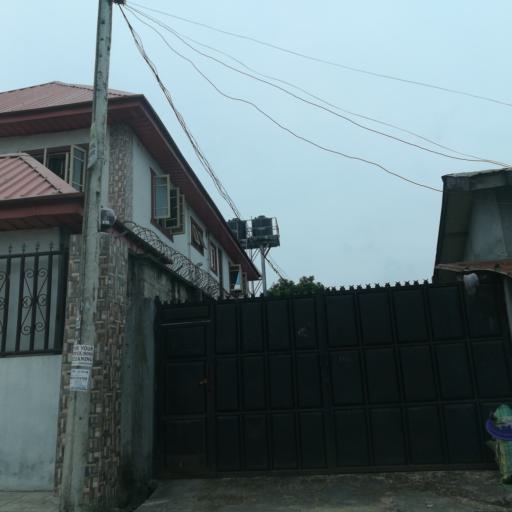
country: NG
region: Rivers
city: Port Harcourt
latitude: 4.8227
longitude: 7.0592
